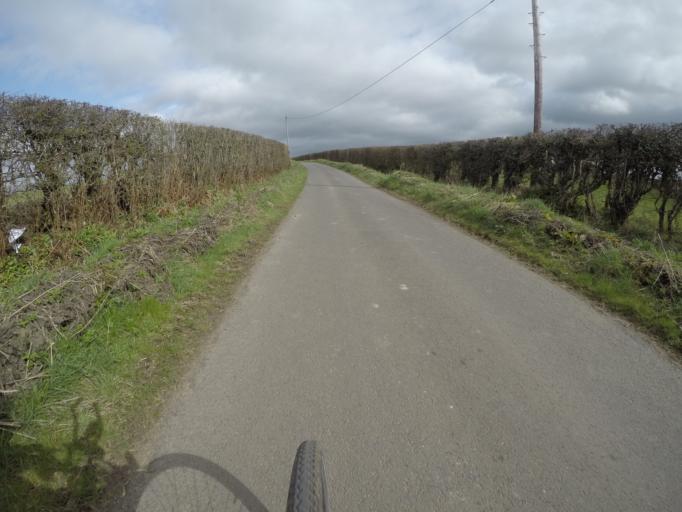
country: GB
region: Scotland
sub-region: North Ayrshire
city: Springside
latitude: 55.6438
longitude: -4.6239
